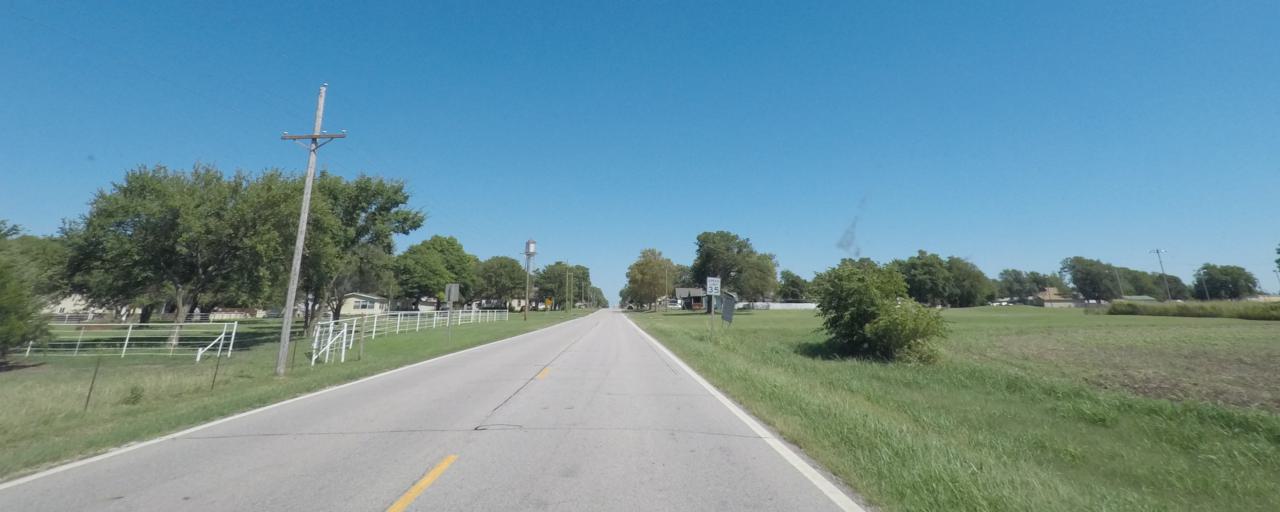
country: US
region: Kansas
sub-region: Sumner County
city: Caldwell
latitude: 37.0446
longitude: -97.4011
